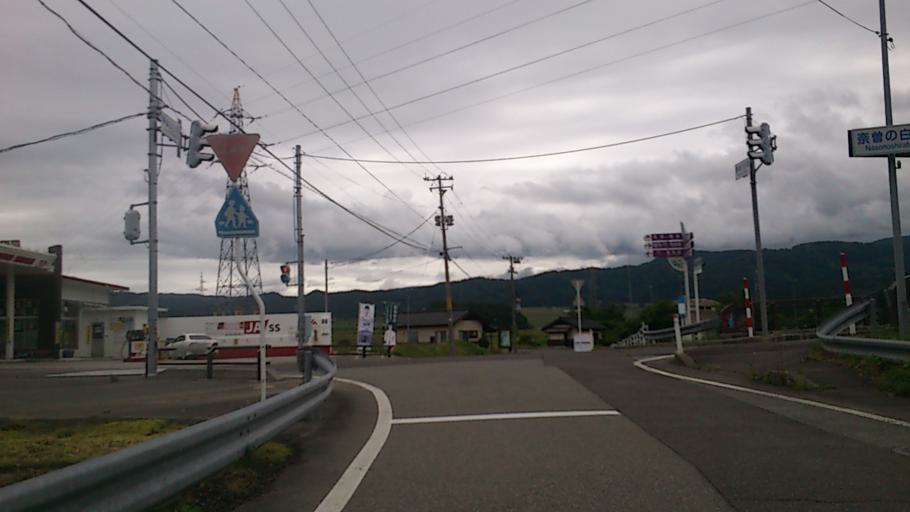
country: JP
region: Yamagata
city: Yuza
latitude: 39.1816
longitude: 139.9454
